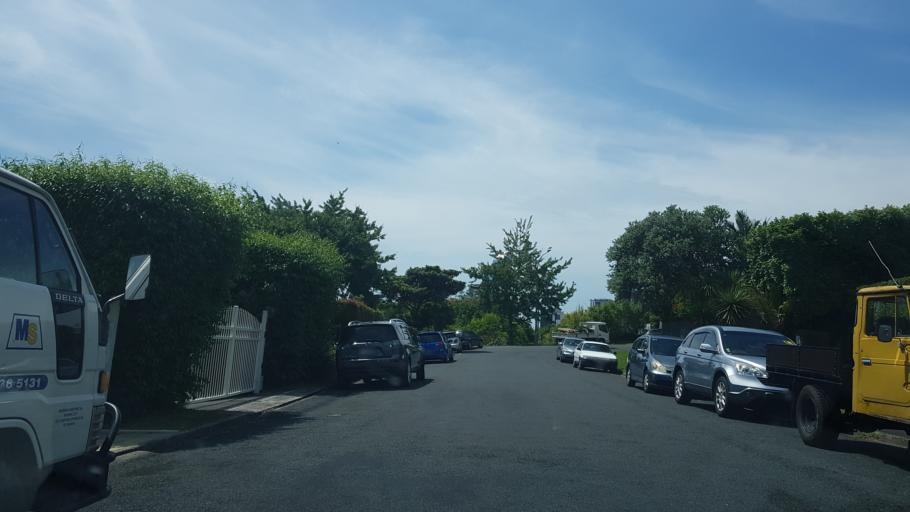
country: NZ
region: Auckland
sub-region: Auckland
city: North Shore
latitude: -36.7860
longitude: 174.7630
